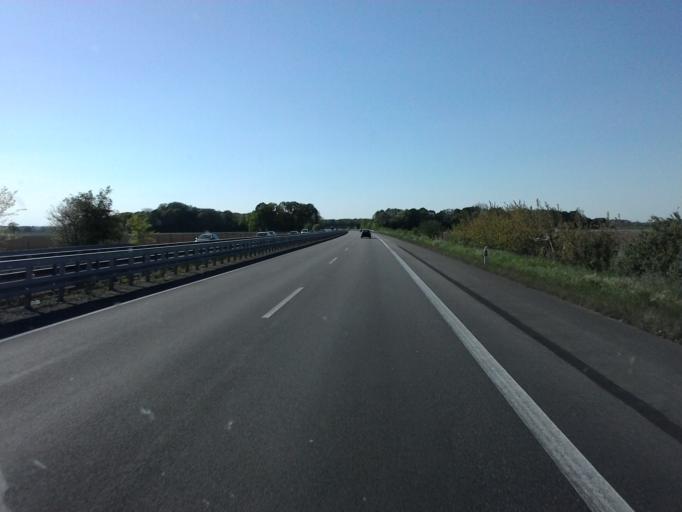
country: DE
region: North Rhine-Westphalia
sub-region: Regierungsbezirk Dusseldorf
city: Mehrhoog
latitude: 51.7709
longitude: 6.5373
